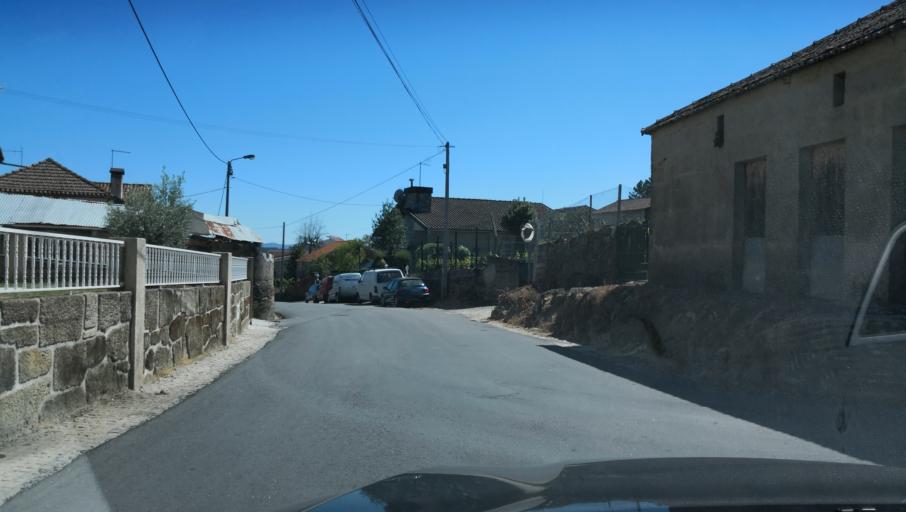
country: PT
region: Vila Real
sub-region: Vila Real
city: Vila Real
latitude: 41.2823
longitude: -7.6840
